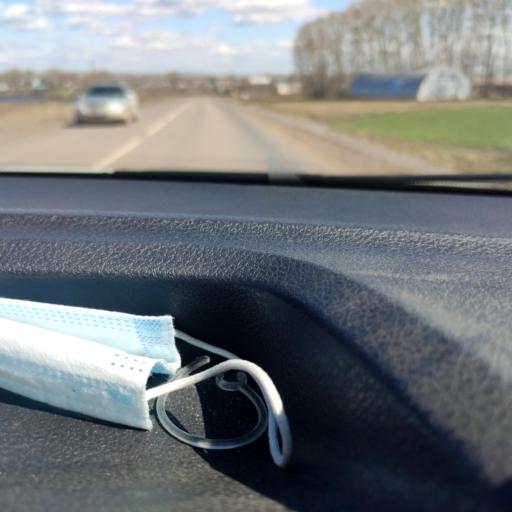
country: RU
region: Bashkortostan
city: Alekseyevka
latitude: 54.7254
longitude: 55.1721
